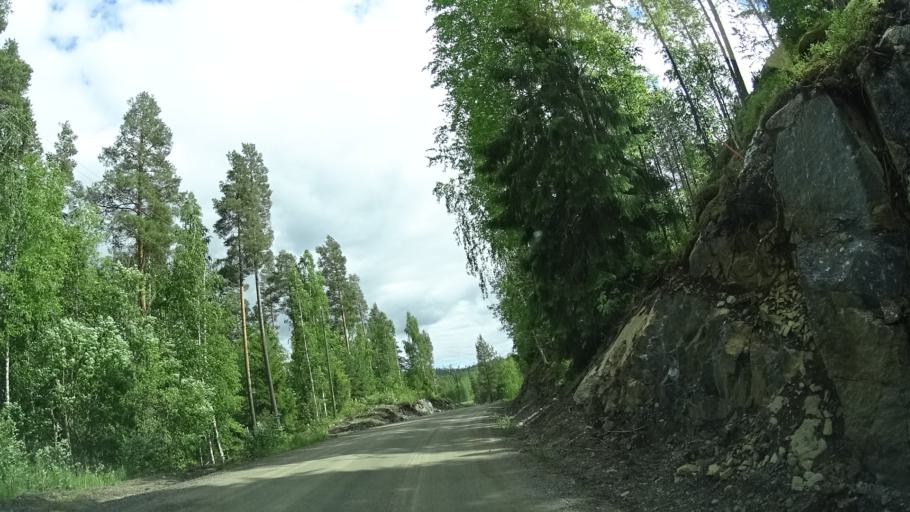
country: FI
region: Central Finland
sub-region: Joutsa
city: Luhanka
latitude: 61.6882
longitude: 25.6754
